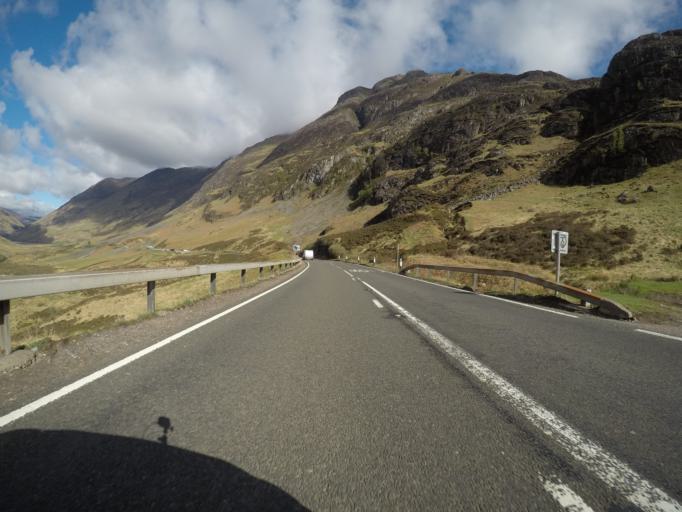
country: GB
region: Scotland
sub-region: Highland
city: Fort William
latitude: 56.6667
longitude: -4.9826
